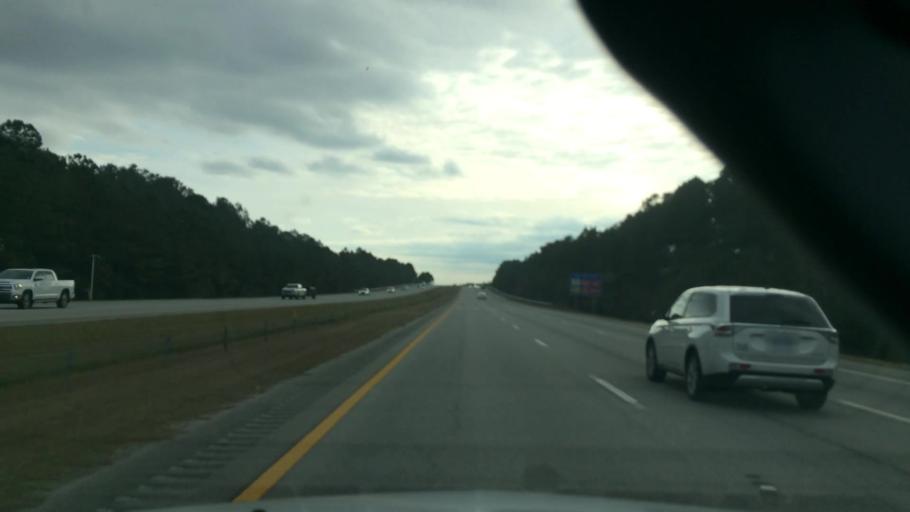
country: US
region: South Carolina
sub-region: Horry County
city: North Myrtle Beach
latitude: 33.8578
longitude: -78.6966
